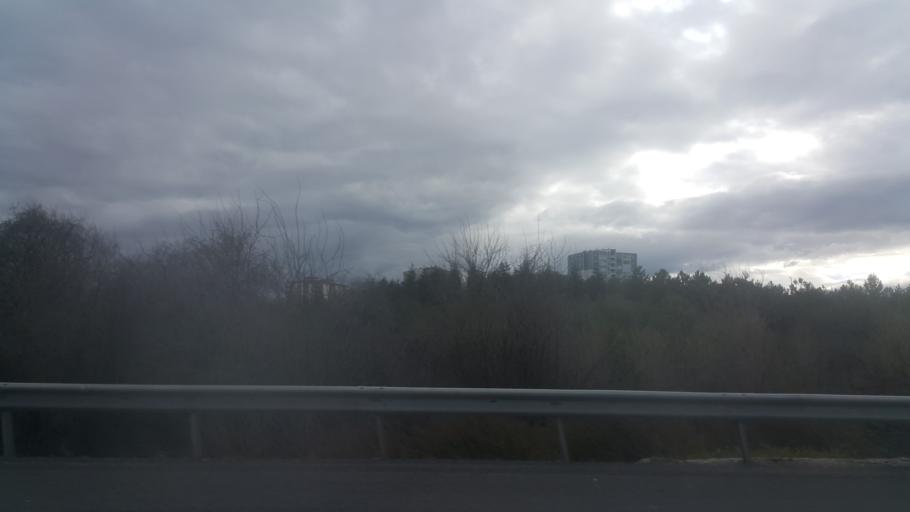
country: TR
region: Ankara
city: Etimesgut
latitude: 40.0129
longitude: 32.6281
